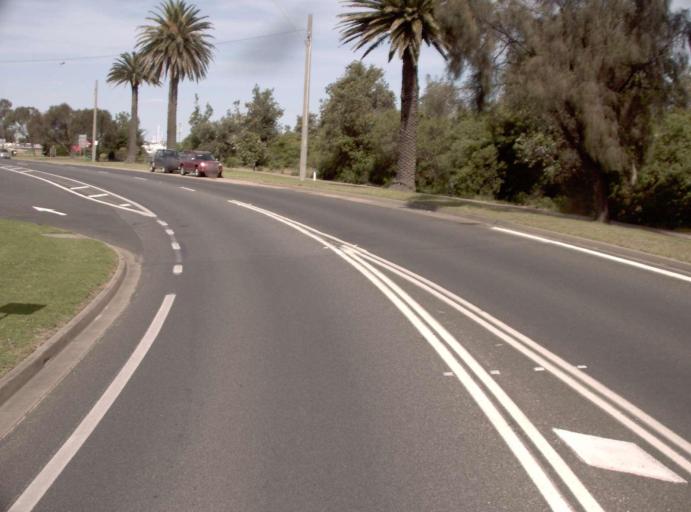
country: AU
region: Victoria
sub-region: East Gippsland
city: Lakes Entrance
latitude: -37.8830
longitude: 147.9740
